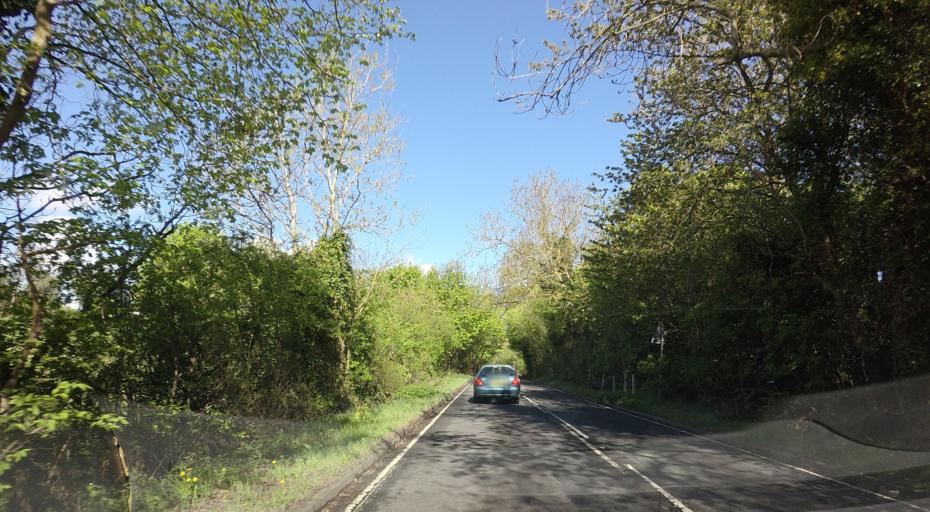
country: GB
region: Scotland
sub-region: West Lothian
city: Broxburn
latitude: 55.9765
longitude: -3.5064
